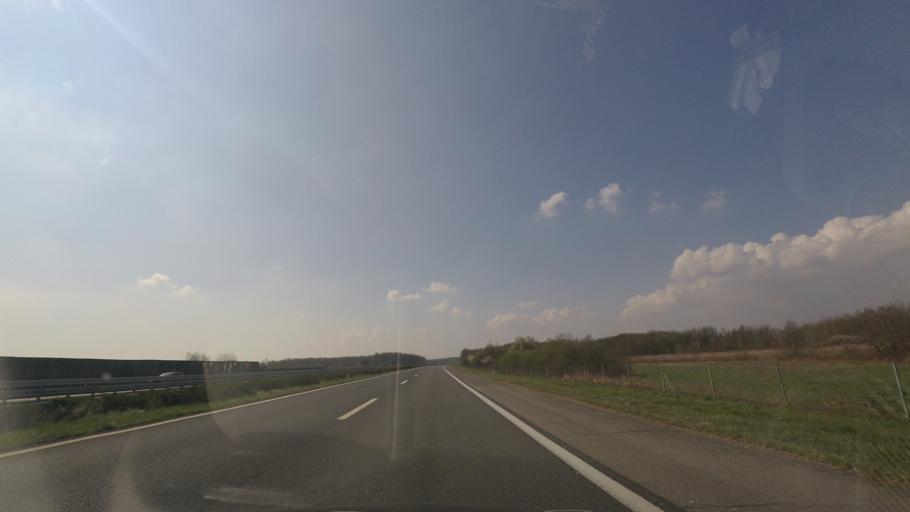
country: HR
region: Grad Zagreb
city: Brezovica
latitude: 45.7326
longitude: 15.8754
